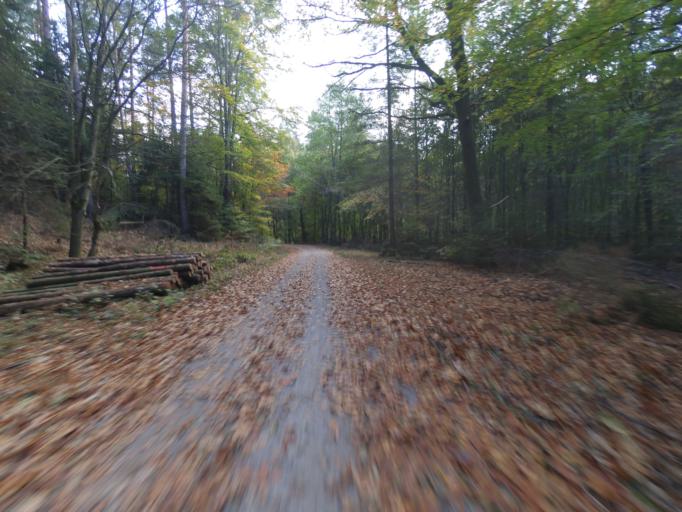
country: DE
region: Saxony
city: Albertstadt
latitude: 51.0996
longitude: 13.8217
